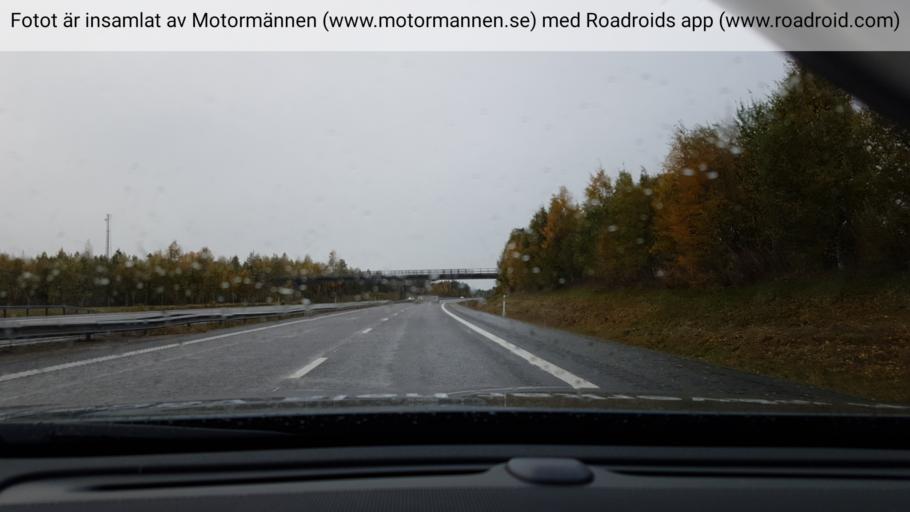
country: SE
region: Norrbotten
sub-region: Pitea Kommun
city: Pitea
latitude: 65.3525
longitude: 21.4370
